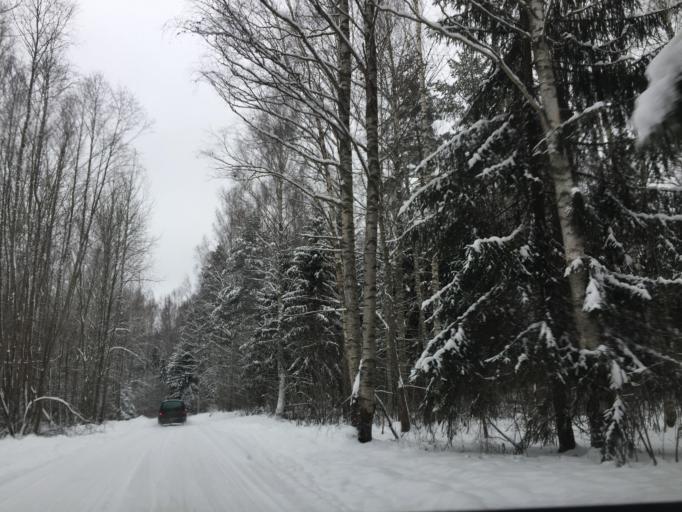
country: LV
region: Smiltene
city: Smiltene
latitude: 57.4004
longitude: 25.9495
